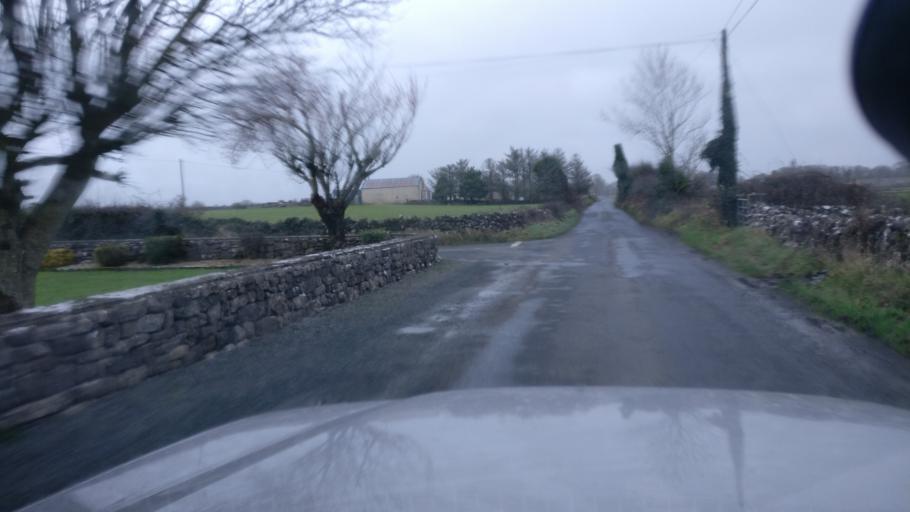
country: IE
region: Connaught
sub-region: County Galway
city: Loughrea
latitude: 53.2312
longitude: -8.6003
